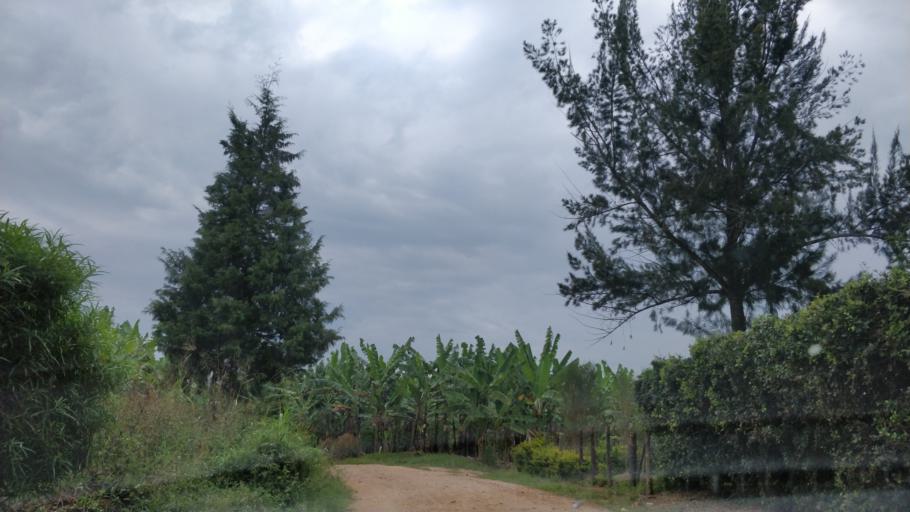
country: UG
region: Western Region
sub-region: Sheema District
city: Kibingo
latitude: -0.6412
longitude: 30.4924
